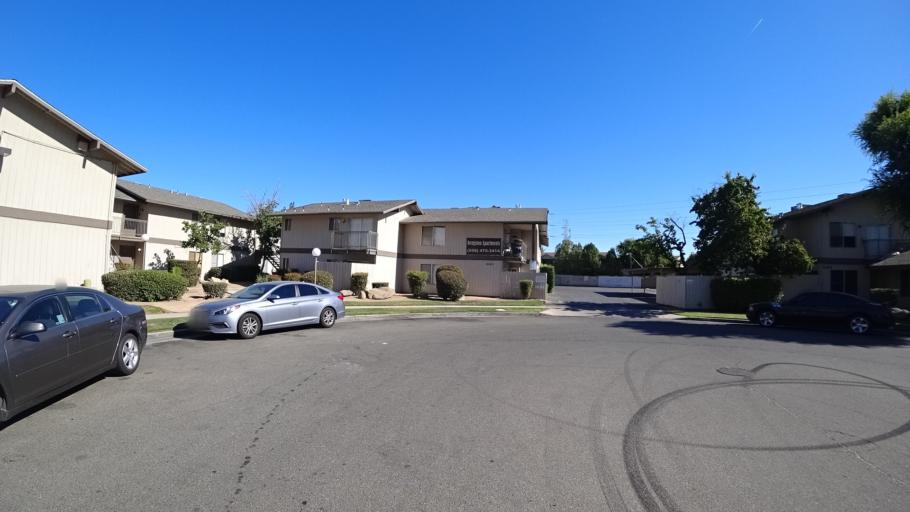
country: US
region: California
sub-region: Fresno County
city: Fresno
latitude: 36.7948
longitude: -119.8304
